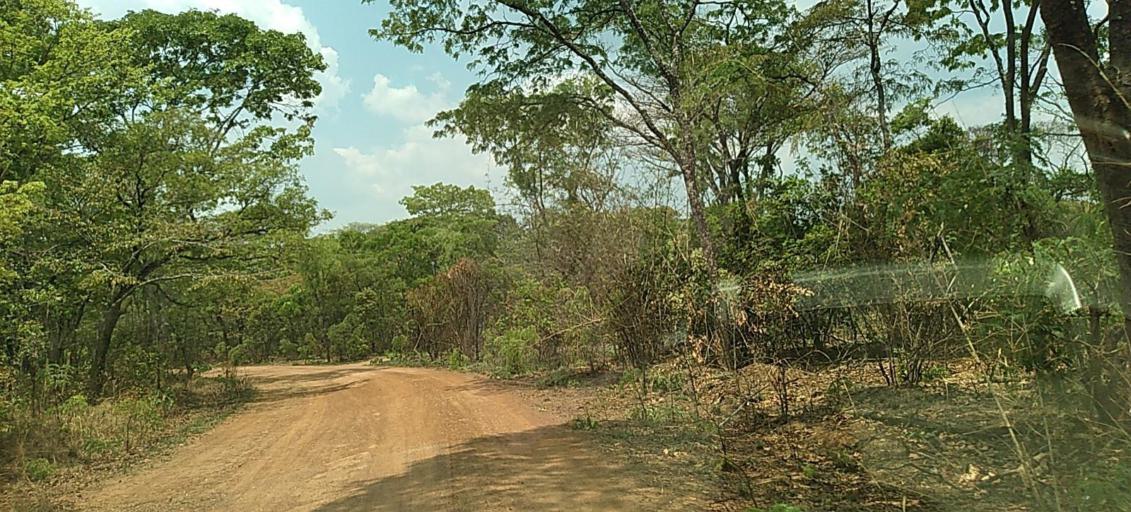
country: ZM
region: Copperbelt
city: Chingola
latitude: -12.7688
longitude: 27.7045
